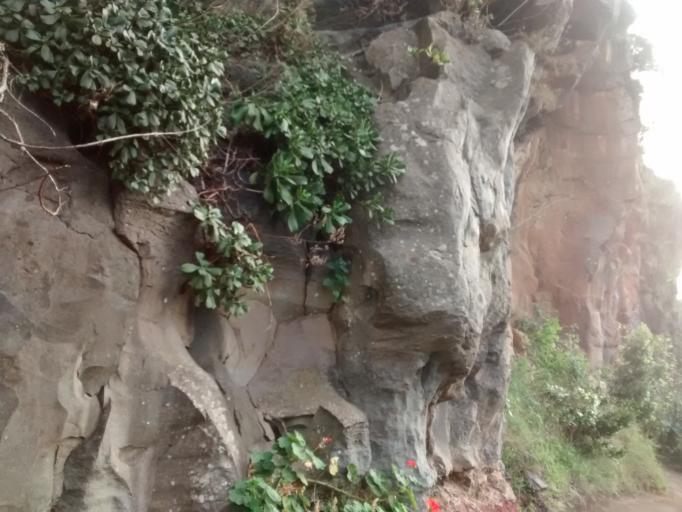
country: PT
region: Madeira
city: Camara de Lobos
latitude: 32.6599
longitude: -16.9605
